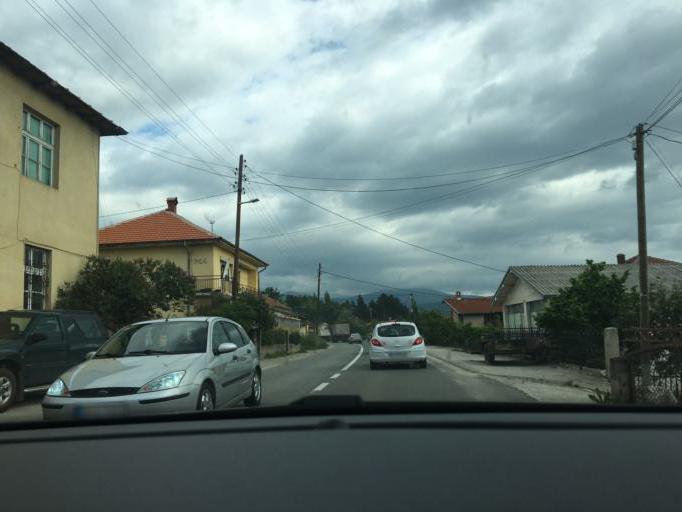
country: MK
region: Resen
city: Jankovec
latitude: 41.1098
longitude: 21.0116
